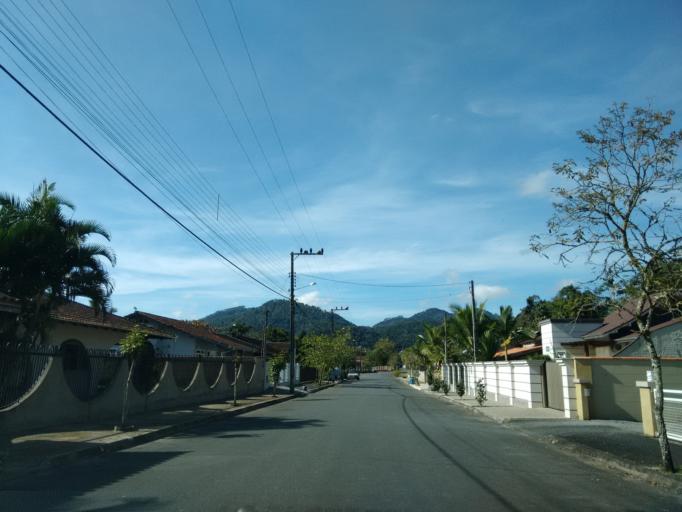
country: BR
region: Santa Catarina
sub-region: Pomerode
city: Pomerode
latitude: -26.7558
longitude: -49.1793
